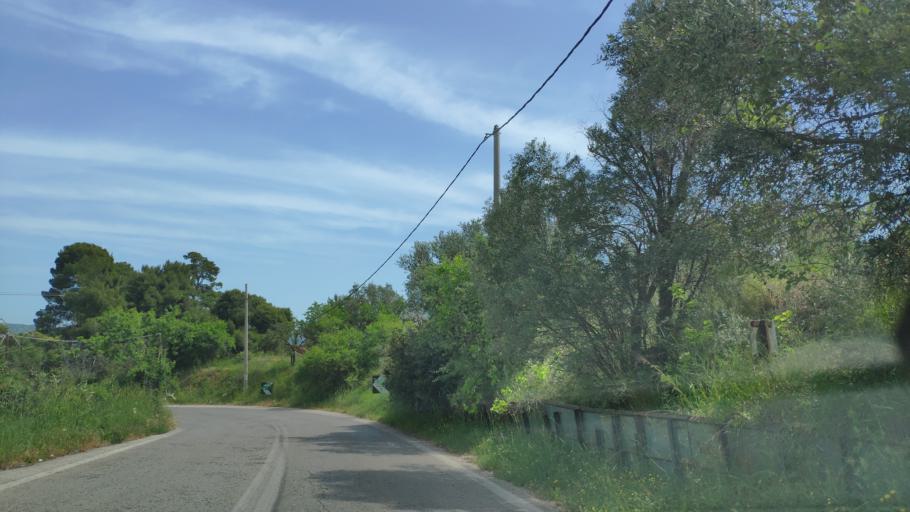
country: GR
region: Attica
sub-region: Nomarchia Anatolikis Attikis
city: Agios Stefanos
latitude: 38.1594
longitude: 23.8611
